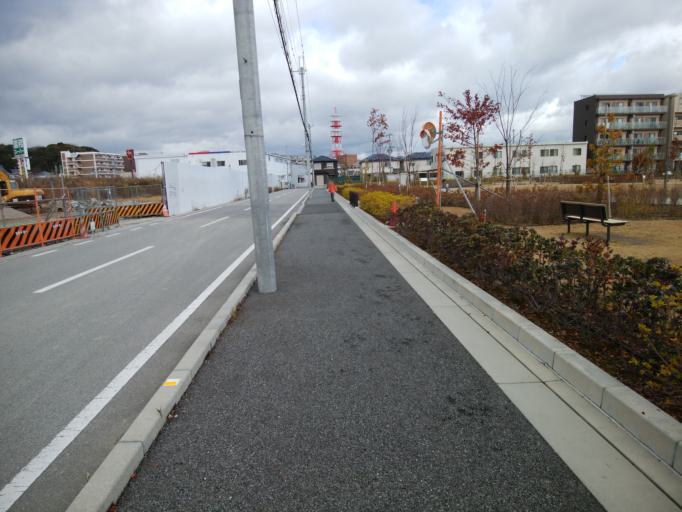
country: JP
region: Hyogo
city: Kawanishi
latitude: 34.8343
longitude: 135.4169
